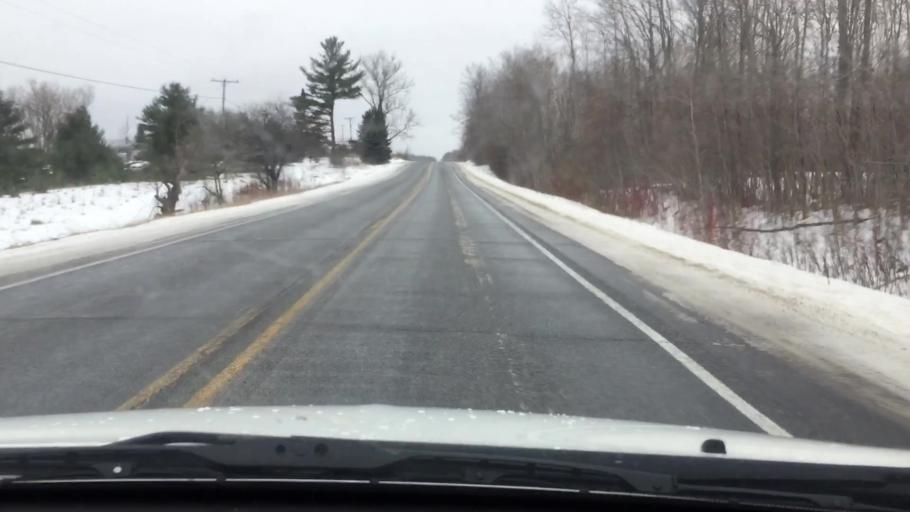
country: US
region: Michigan
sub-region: Wexford County
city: Cadillac
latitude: 44.1113
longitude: -85.4443
